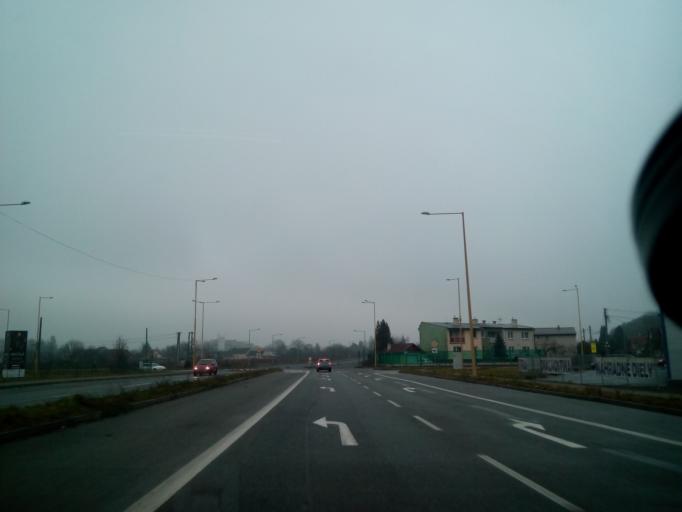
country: SK
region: Presovsky
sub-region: Okres Presov
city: Presov
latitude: 48.9834
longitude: 21.2335
